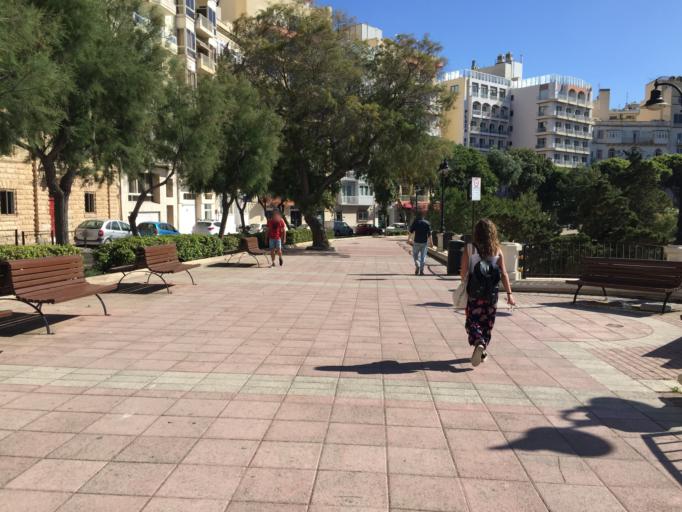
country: MT
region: Tas-Sliema
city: Sliema
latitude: 35.9154
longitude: 14.4980
